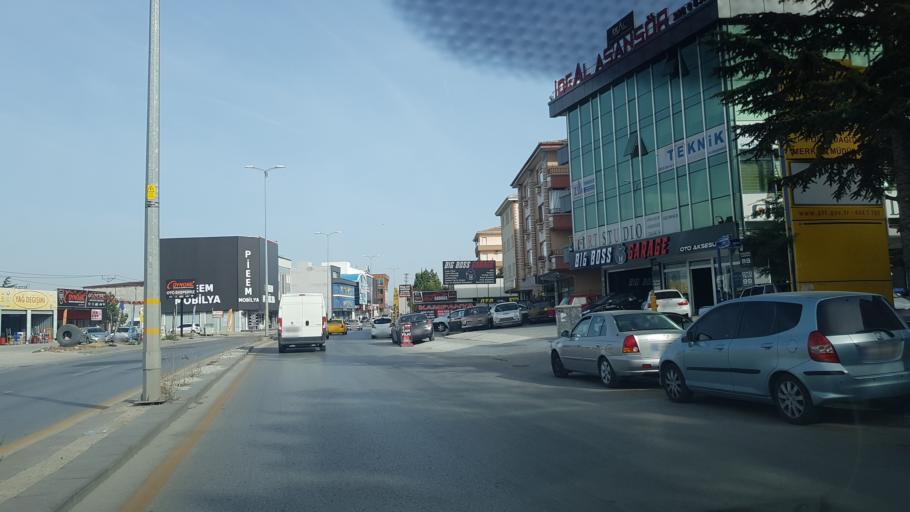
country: TR
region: Ankara
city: Etimesgut
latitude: 39.9528
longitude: 32.6406
